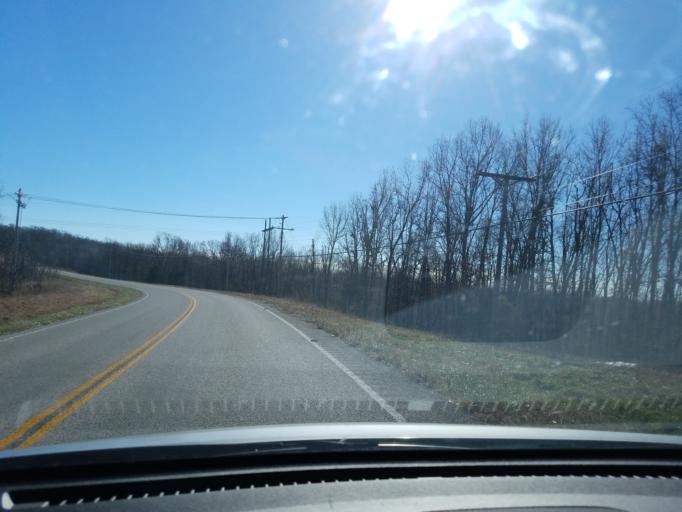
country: US
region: Missouri
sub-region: Taney County
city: Hollister
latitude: 36.5237
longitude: -93.2747
